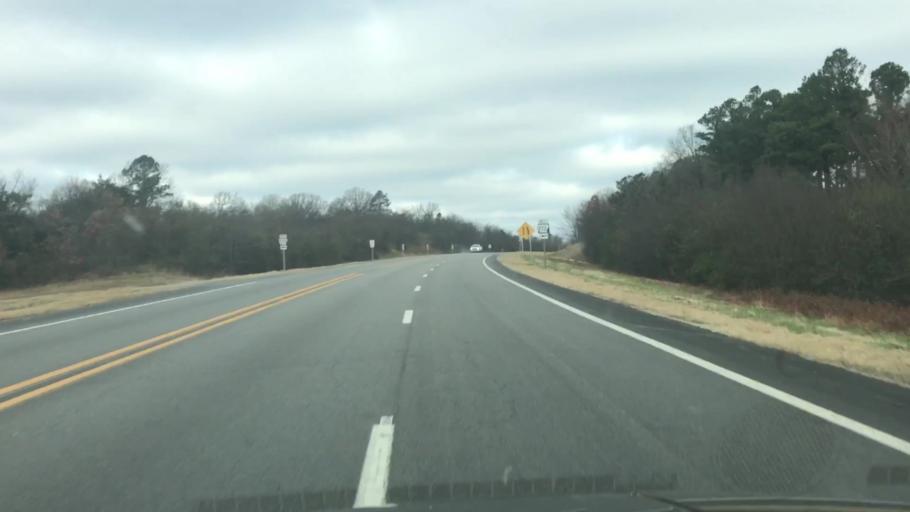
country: US
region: Arkansas
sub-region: Scott County
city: Waldron
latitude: 34.8825
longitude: -94.1045
